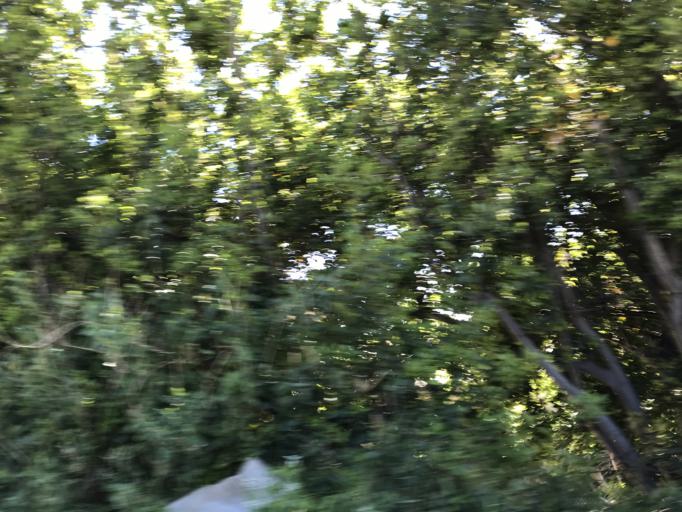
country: TR
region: Hatay
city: Samandag
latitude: 36.1133
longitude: 35.9389
